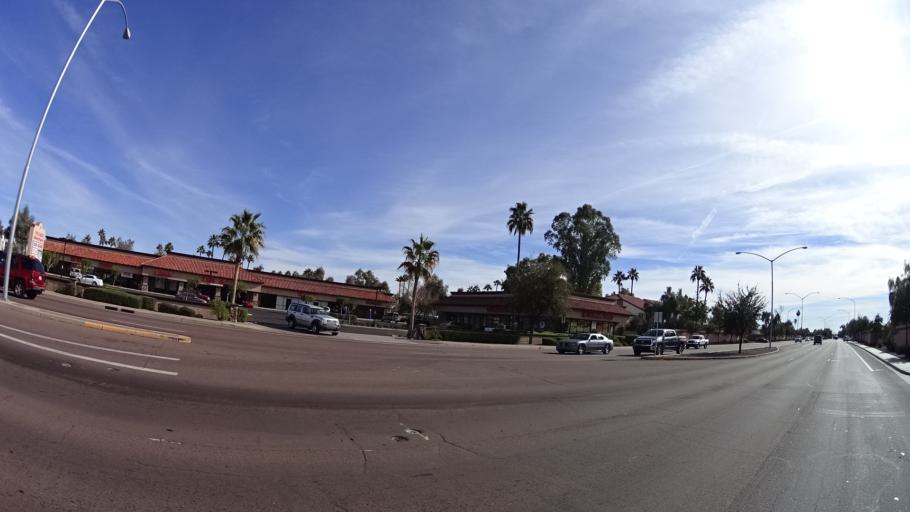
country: US
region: Arizona
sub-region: Maricopa County
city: Mesa
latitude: 33.4062
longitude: -111.7885
